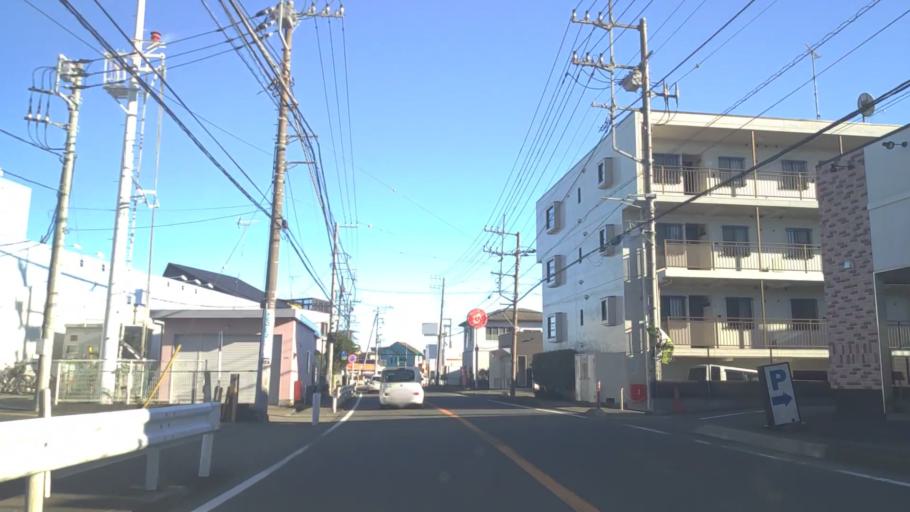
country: JP
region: Kanagawa
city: Chigasaki
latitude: 35.3574
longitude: 139.3937
